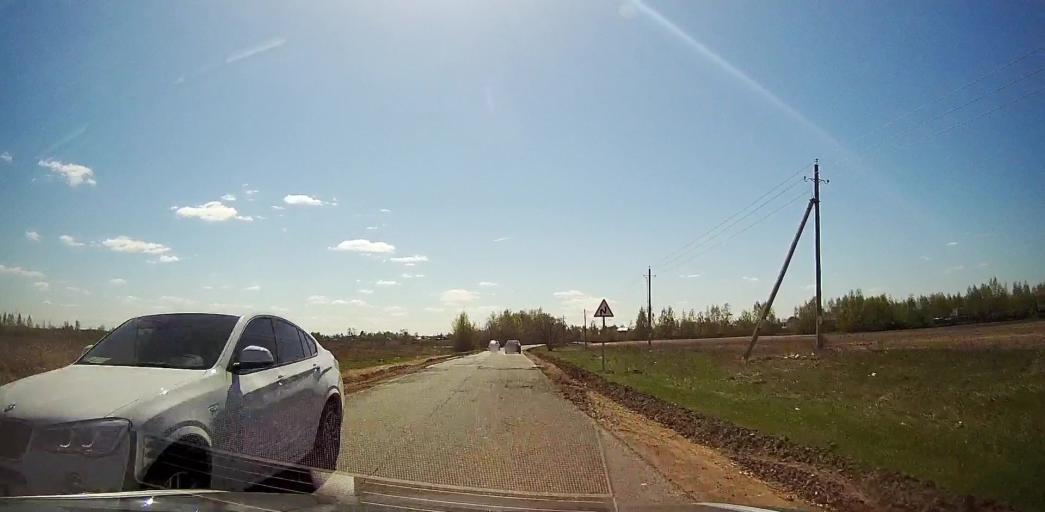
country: RU
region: Moskovskaya
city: Malyshevo
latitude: 55.4636
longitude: 38.3824
